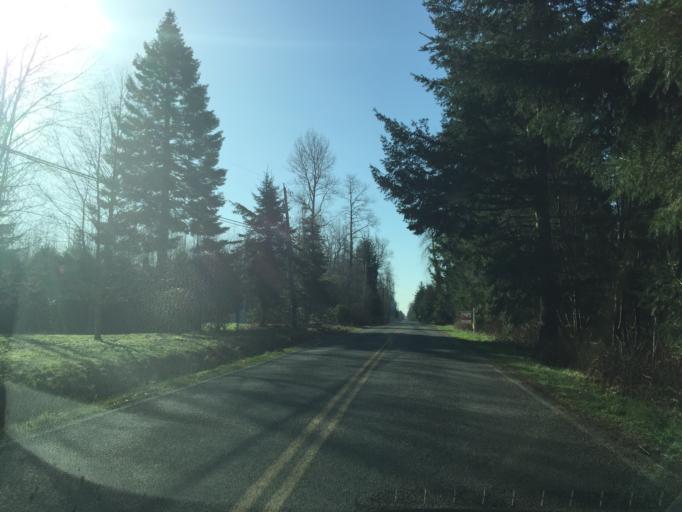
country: US
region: Washington
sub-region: Whatcom County
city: Marietta-Alderwood
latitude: 48.8057
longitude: -122.5081
